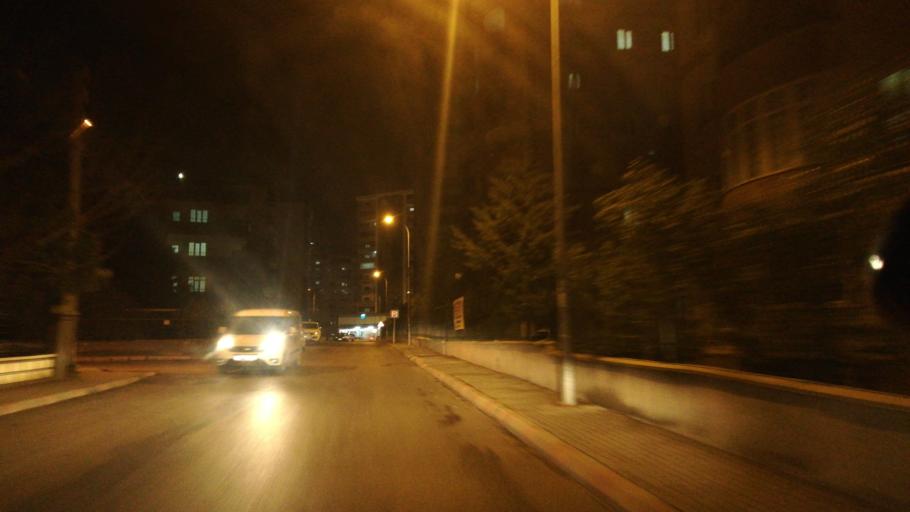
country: TR
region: Kahramanmaras
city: Kahramanmaras
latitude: 37.5876
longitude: 36.8562
